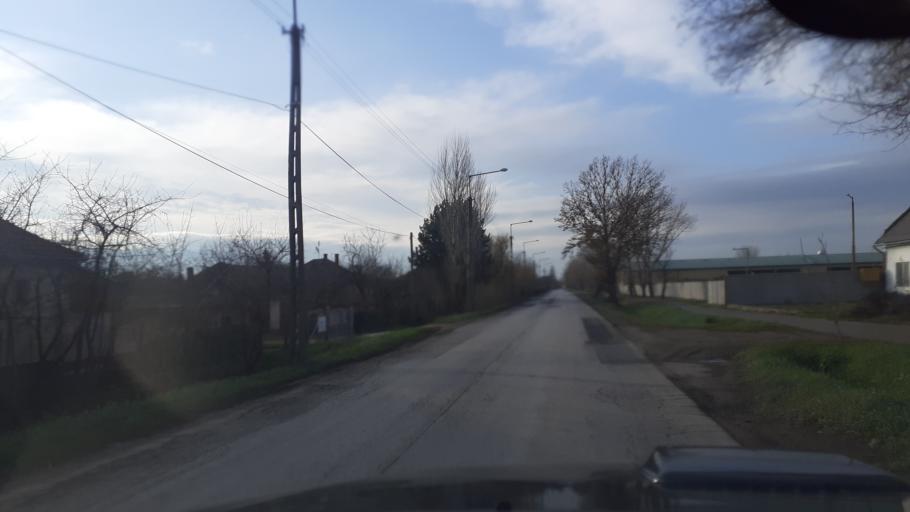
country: HU
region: Bacs-Kiskun
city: Kunszentmiklos
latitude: 47.0227
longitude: 19.1065
